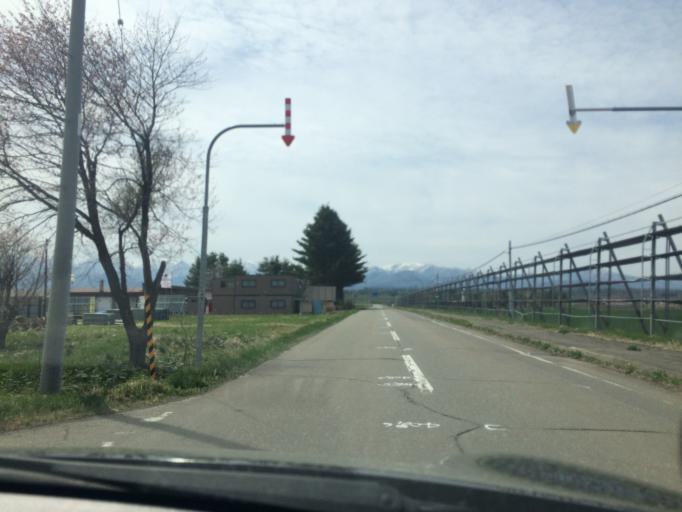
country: JP
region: Hokkaido
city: Otofuke
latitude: 43.0159
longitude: 142.9518
